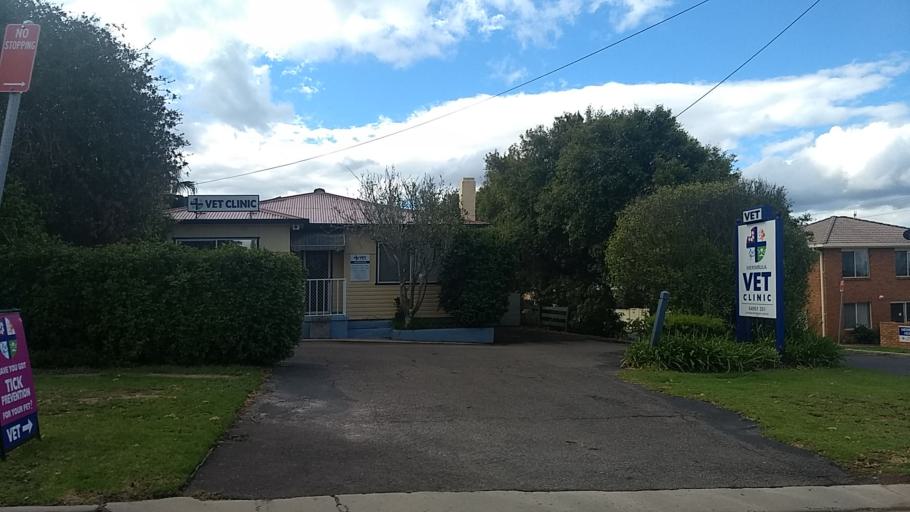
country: AU
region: New South Wales
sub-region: Bega Valley
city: Merimbula
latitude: -36.8887
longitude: 149.9052
